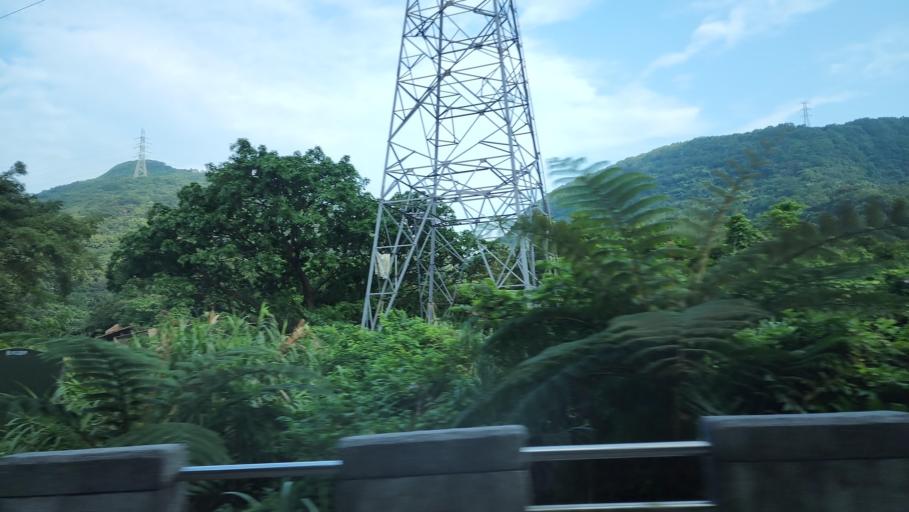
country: TW
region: Taiwan
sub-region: Keelung
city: Keelung
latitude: 25.1928
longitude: 121.6437
